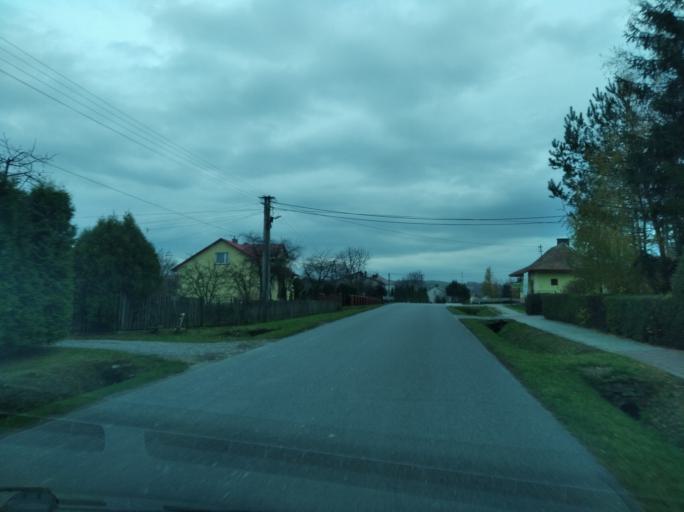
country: PL
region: Subcarpathian Voivodeship
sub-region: Powiat ropczycko-sedziszowski
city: Iwierzyce
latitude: 50.0064
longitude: 21.7555
